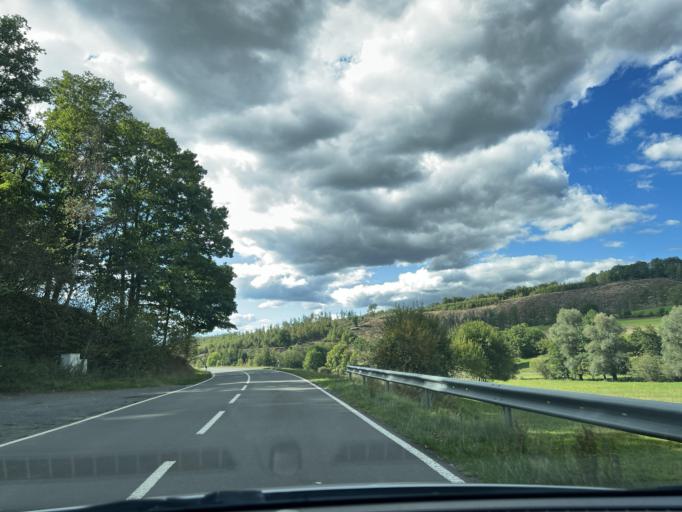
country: DE
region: North Rhine-Westphalia
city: Hilchenbach
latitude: 50.9716
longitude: 8.1234
